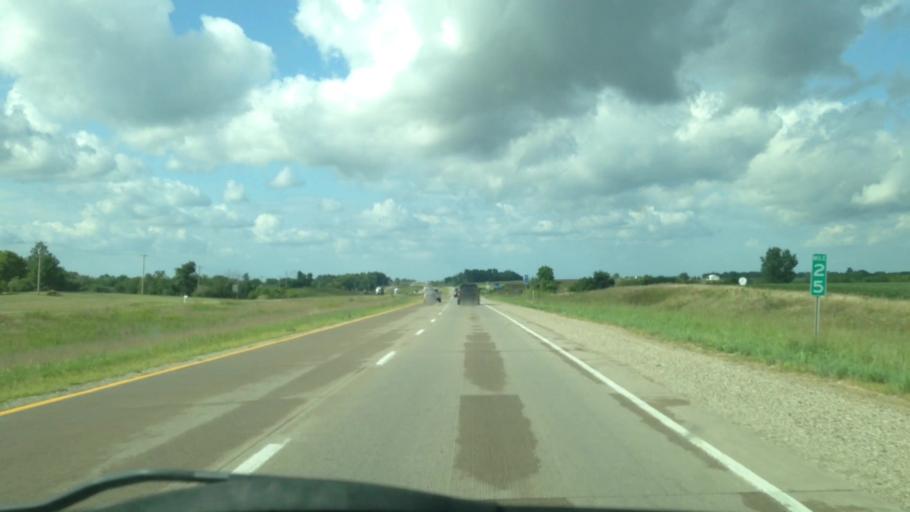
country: US
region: Iowa
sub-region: Henry County
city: Mount Pleasant
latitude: 40.7198
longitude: -91.5635
